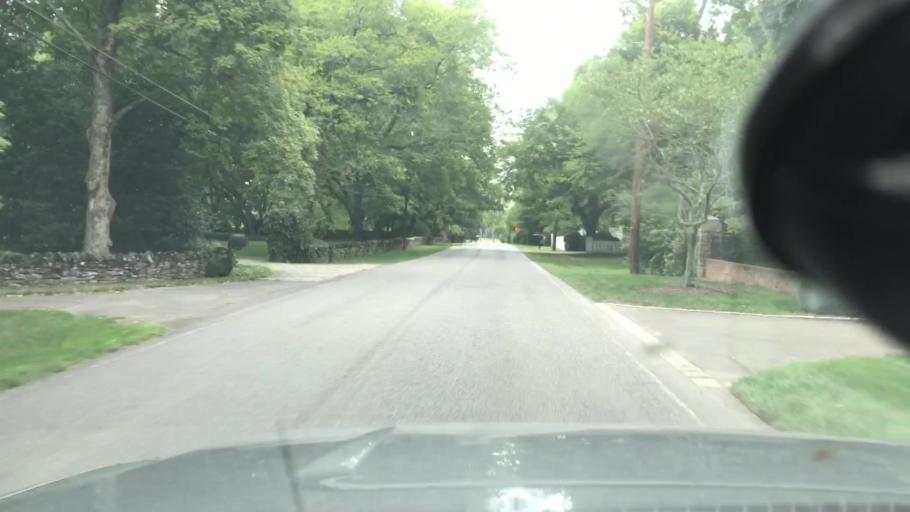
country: US
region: Tennessee
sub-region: Davidson County
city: Belle Meade
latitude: 36.0890
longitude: -86.8574
